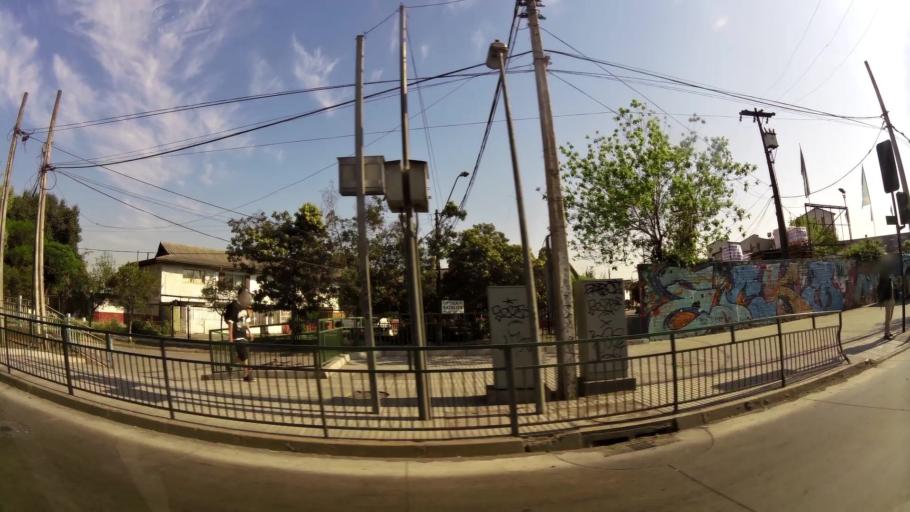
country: CL
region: Santiago Metropolitan
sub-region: Provincia de Santiago
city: Lo Prado
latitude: -33.5113
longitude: -70.7262
